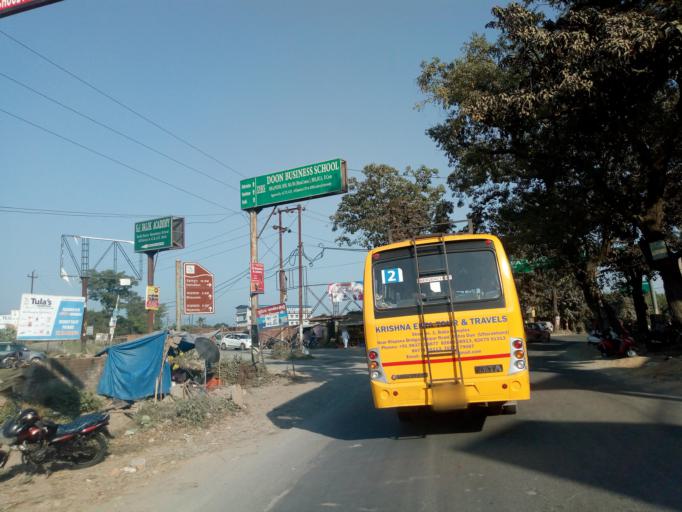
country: IN
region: Uttarakhand
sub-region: Dehradun
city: Vikasnagar
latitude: 30.3512
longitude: 77.8647
